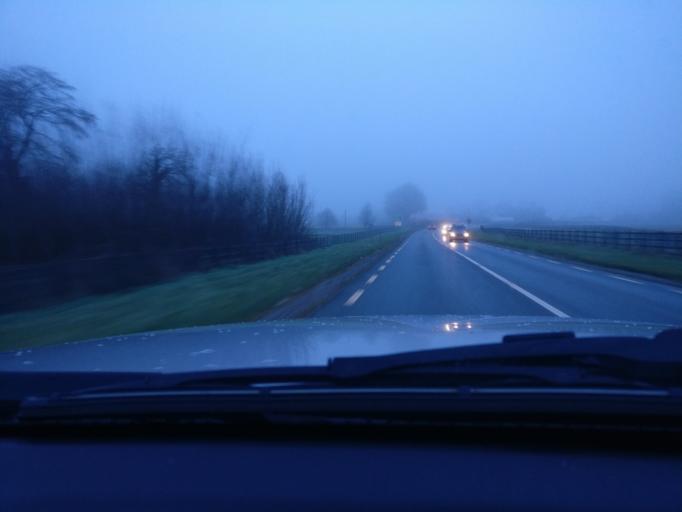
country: IE
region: Leinster
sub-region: An Mhi
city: Athboy
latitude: 53.6357
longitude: -6.8944
